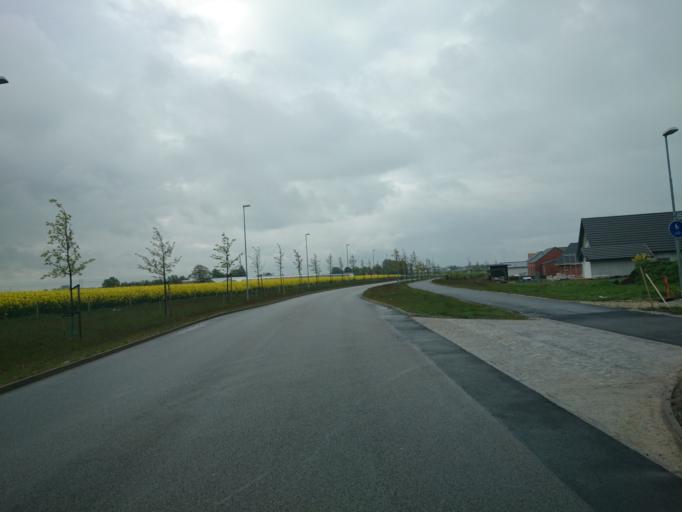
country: SE
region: Skane
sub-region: Malmo
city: Bunkeflostrand
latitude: 55.5477
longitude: 12.9287
